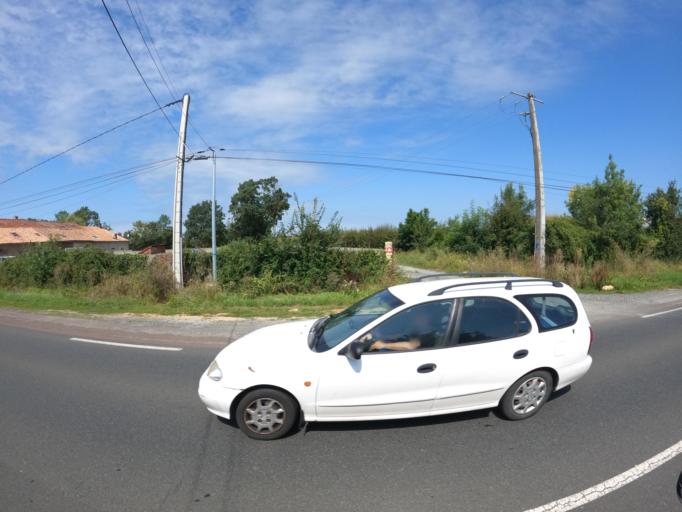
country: FR
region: Poitou-Charentes
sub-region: Departement des Deux-Sevres
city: Bessines
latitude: 46.2861
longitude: -0.5135
